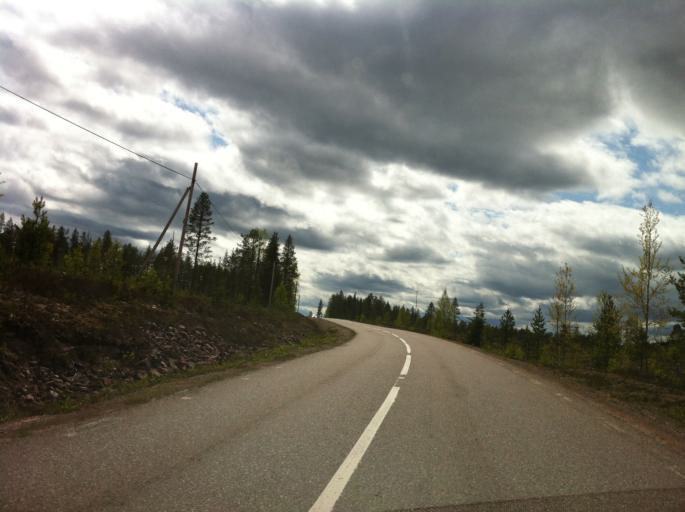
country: NO
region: Hedmark
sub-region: Trysil
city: Innbygda
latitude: 61.6792
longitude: 13.1259
